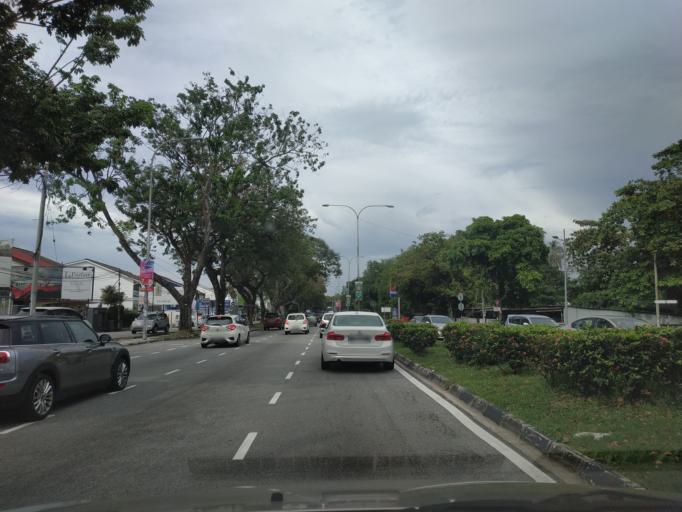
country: MY
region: Penang
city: George Town
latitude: 5.3925
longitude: 100.3026
